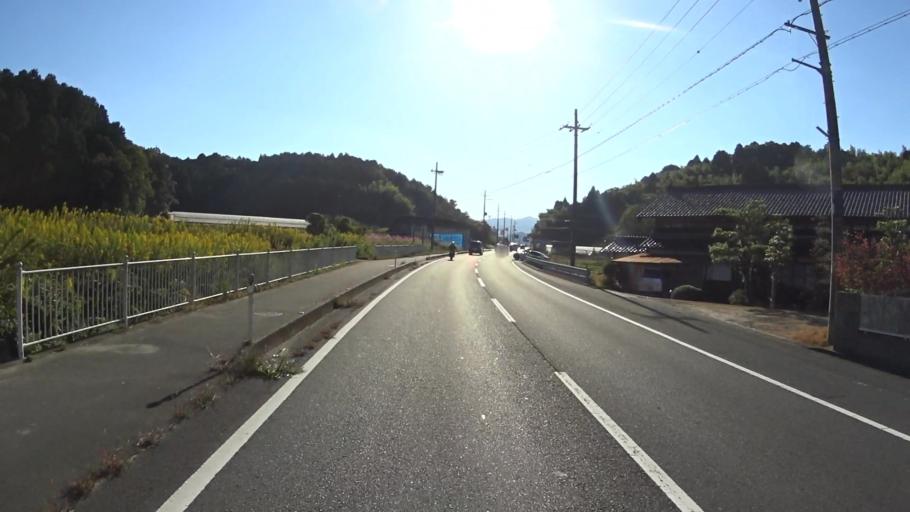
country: JP
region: Kyoto
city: Miyazu
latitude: 35.5257
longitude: 135.1160
